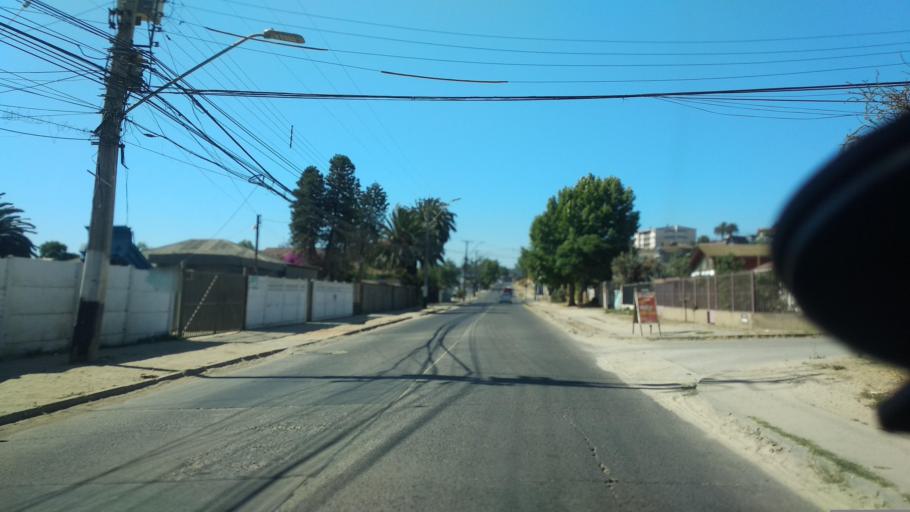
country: CL
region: Valparaiso
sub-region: Provincia de Marga Marga
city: Villa Alemana
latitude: -33.0534
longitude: -71.3740
